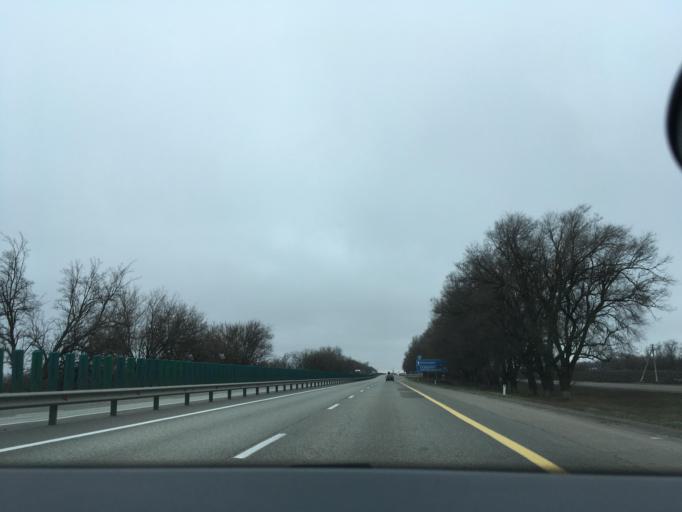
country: RU
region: Krasnodarskiy
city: Krasnoye
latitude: 46.6929
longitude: 39.6517
